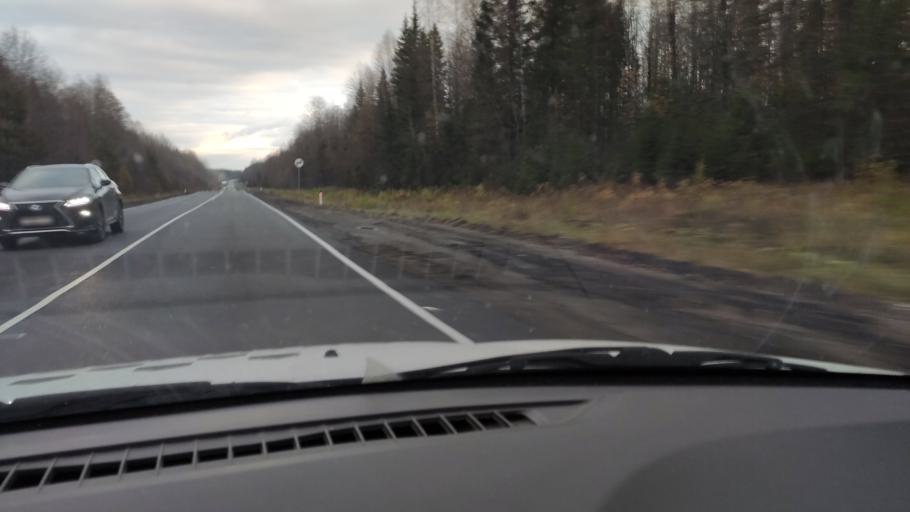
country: RU
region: Kirov
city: Omutninsk
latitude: 58.7582
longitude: 52.0229
